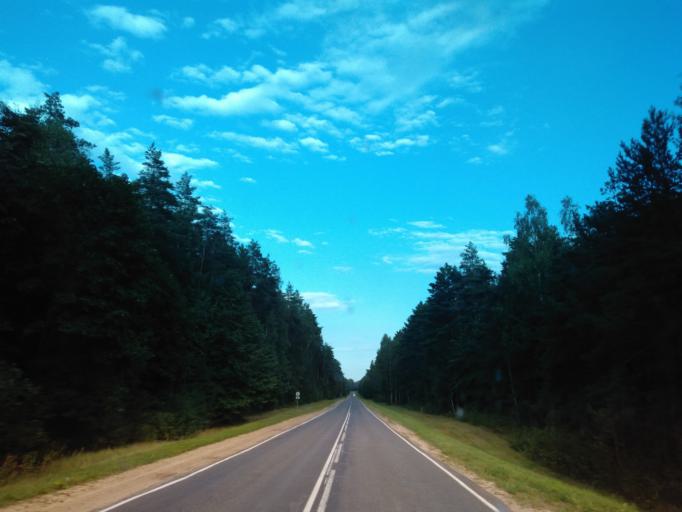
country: BY
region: Minsk
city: Uzda
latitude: 53.4250
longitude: 27.3748
